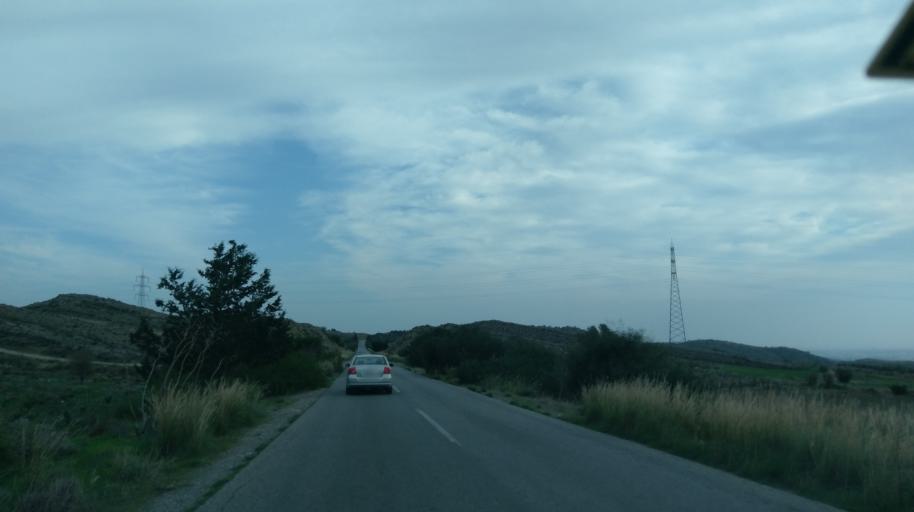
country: CY
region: Lefkosia
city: Nicosia
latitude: 35.2575
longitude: 33.3902
